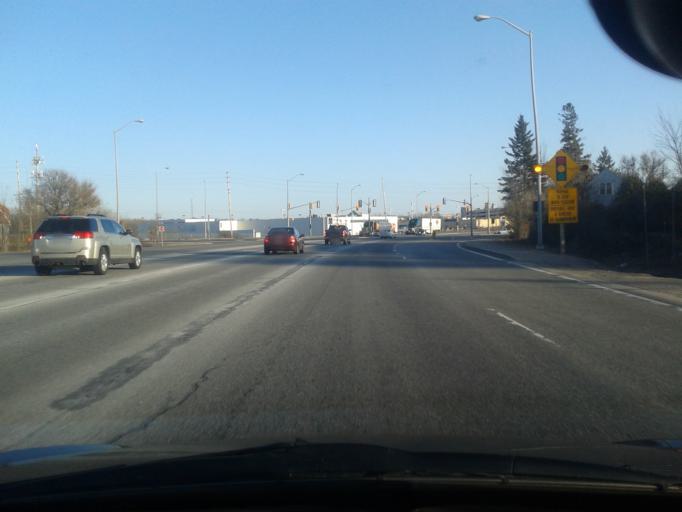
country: CA
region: Ontario
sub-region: Nipissing District
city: North Bay
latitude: 46.3194
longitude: -79.4442
